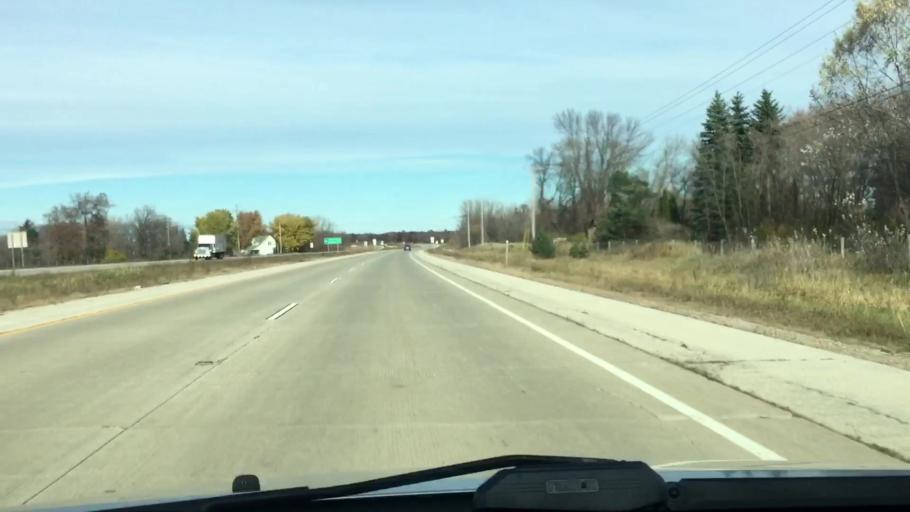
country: US
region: Wisconsin
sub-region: Brown County
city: Bellevue
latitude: 44.5793
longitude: -87.8723
